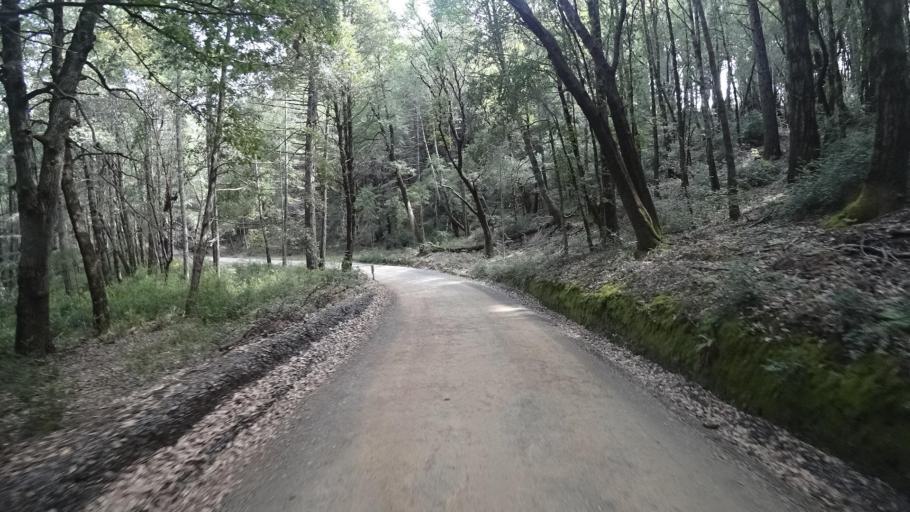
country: US
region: California
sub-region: Humboldt County
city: Redway
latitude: 40.0408
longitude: -123.8486
